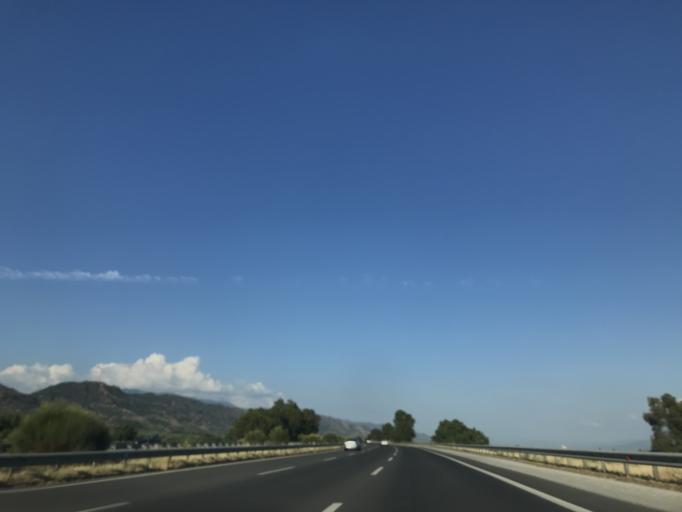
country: TR
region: Aydin
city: Germencik
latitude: 37.8692
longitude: 27.6549
